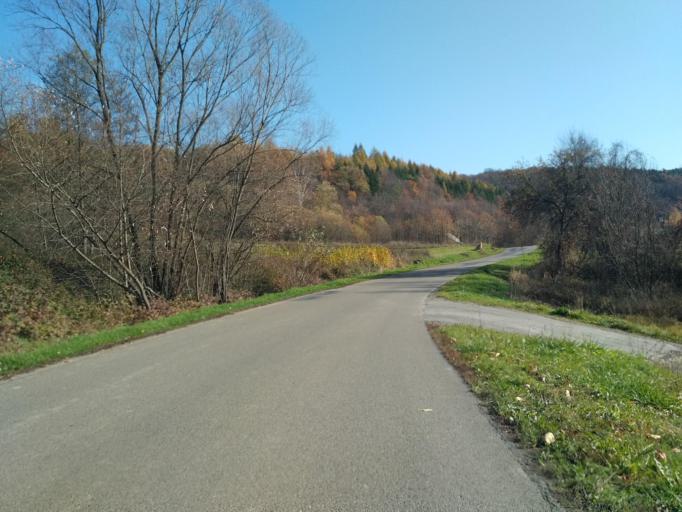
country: PL
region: Subcarpathian Voivodeship
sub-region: Powiat brzozowski
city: Nozdrzec
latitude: 49.7929
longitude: 22.2052
